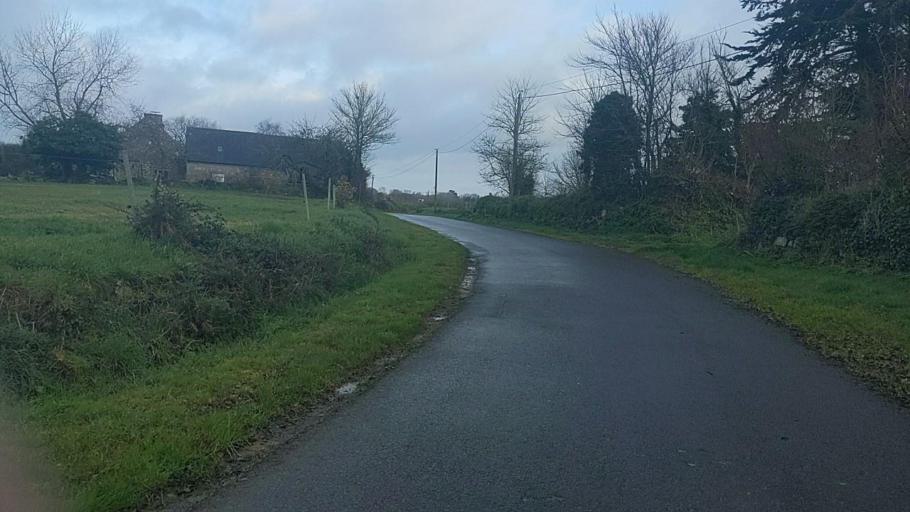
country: FR
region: Brittany
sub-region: Departement des Cotes-d'Armor
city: Plougrescant
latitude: 48.8325
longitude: -3.1866
